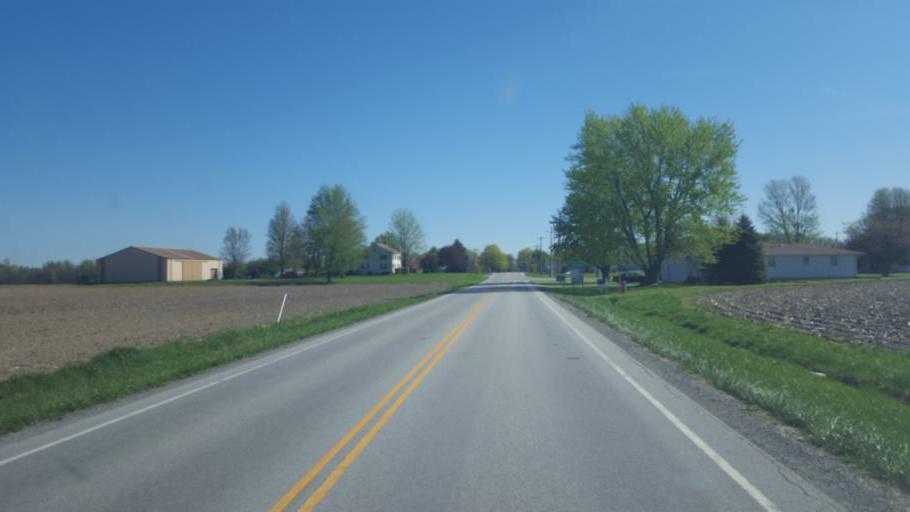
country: US
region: Ohio
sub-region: Wyandot County
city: Upper Sandusky
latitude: 40.9475
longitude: -83.1804
